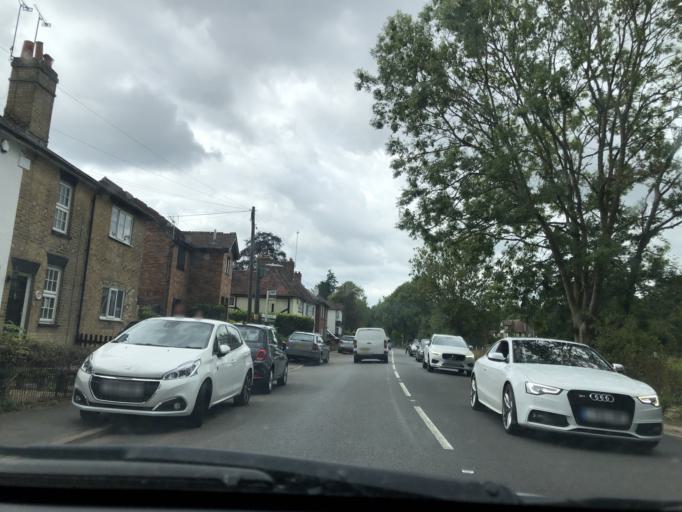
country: GB
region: England
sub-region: Kent
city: Halstead
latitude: 51.2780
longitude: 0.1209
